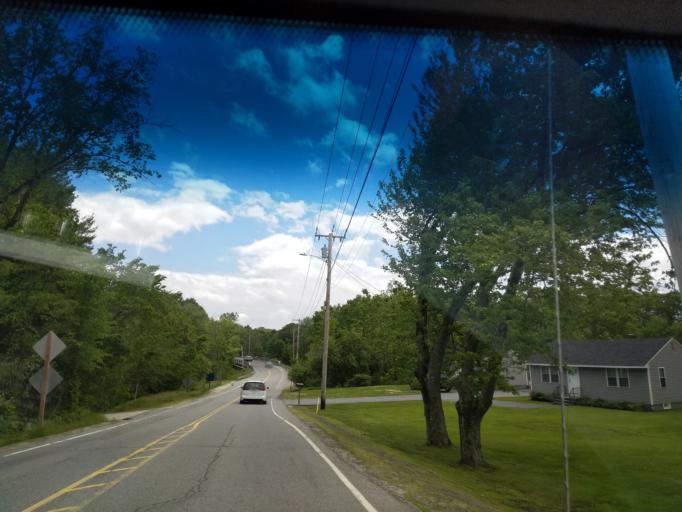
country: US
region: Maine
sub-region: Cumberland County
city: Falmouth
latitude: 43.7400
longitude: -70.2883
